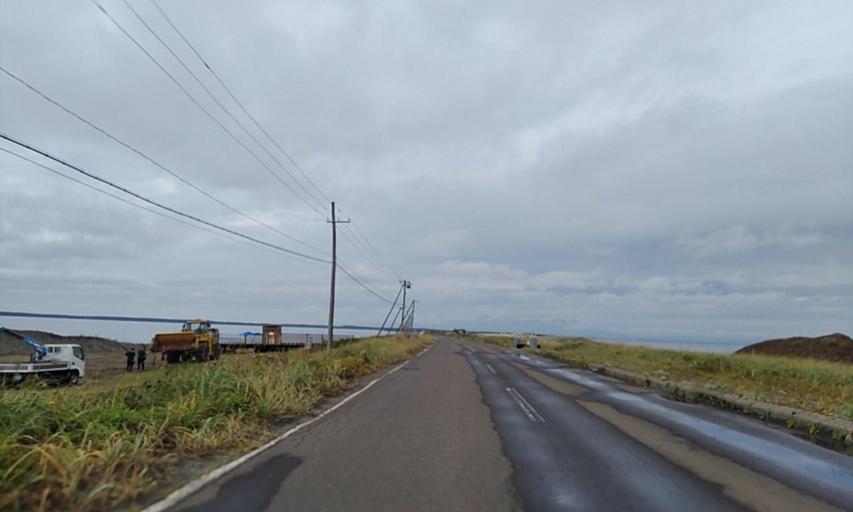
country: JP
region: Hokkaido
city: Shibetsu
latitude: 43.6128
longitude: 145.2567
